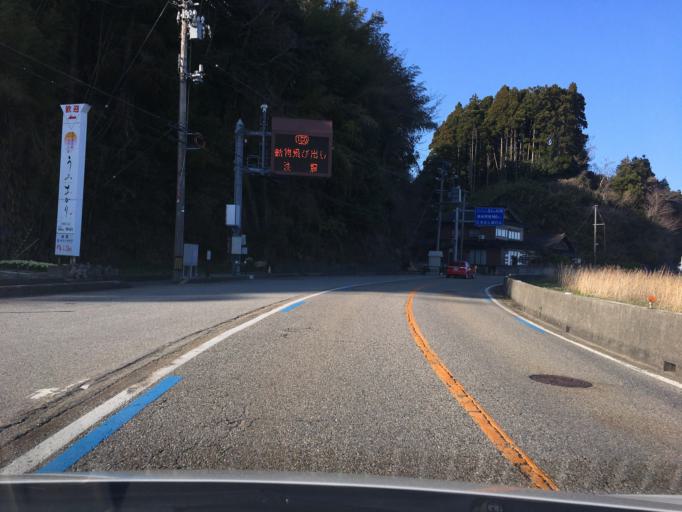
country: JP
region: Toyama
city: Himi
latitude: 36.9064
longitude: 137.0146
